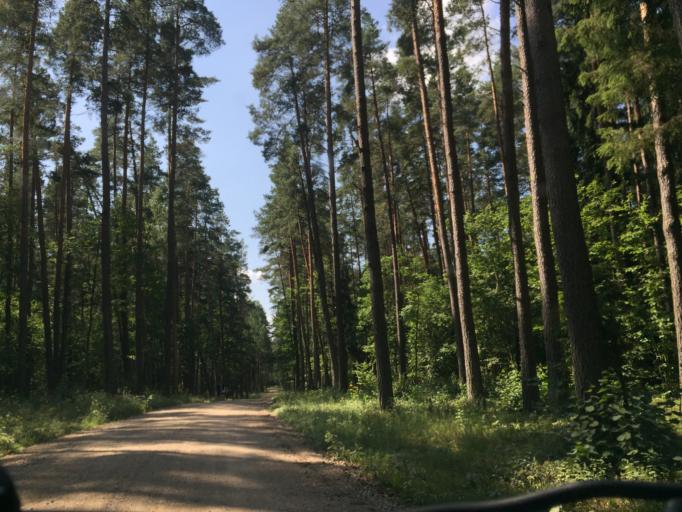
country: LV
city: Tervete
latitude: 56.4922
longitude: 23.4049
